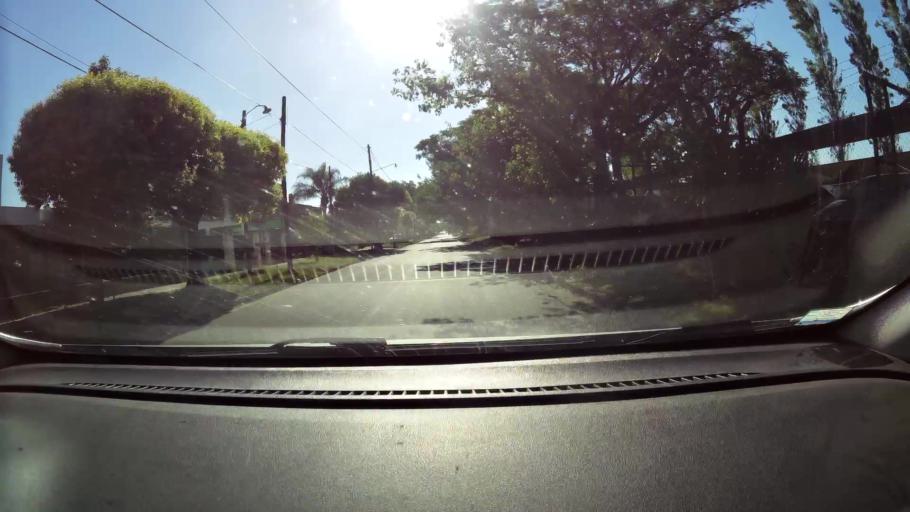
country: AR
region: Cordoba
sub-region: Departamento de Capital
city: Cordoba
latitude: -31.3575
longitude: -64.1980
